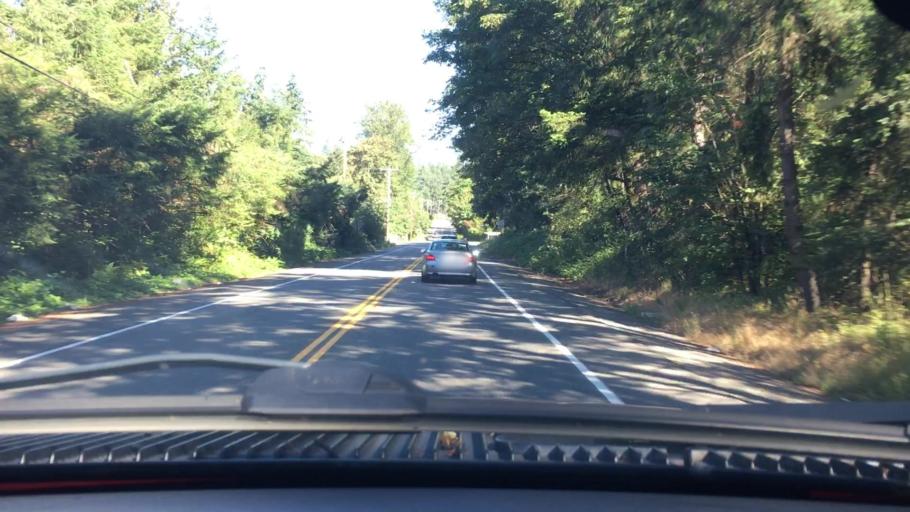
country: US
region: Washington
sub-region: King County
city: Covington
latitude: 47.3422
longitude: -122.1322
